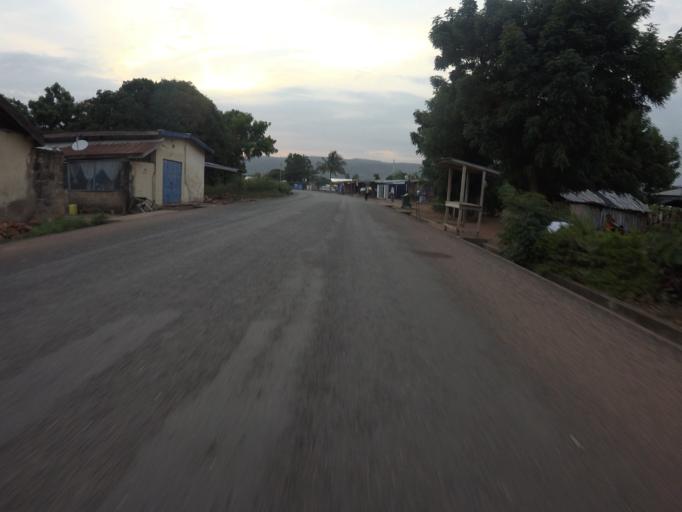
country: GH
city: Akropong
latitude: 6.1013
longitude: -0.0101
